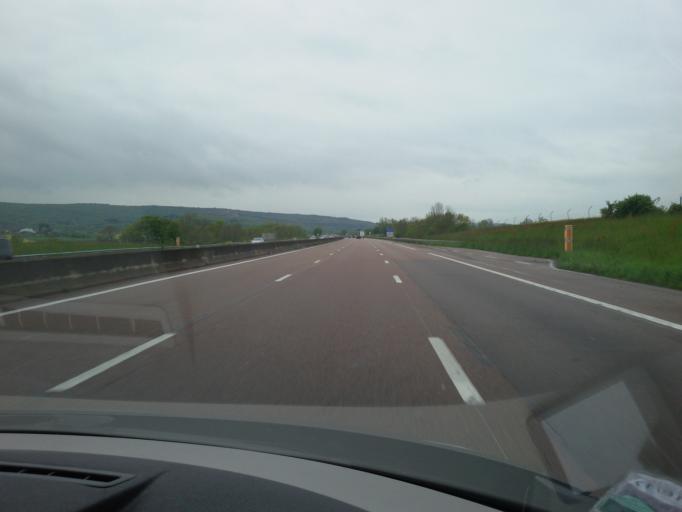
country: FR
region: Bourgogne
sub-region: Departement de Saone-et-Loire
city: Tournus
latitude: 46.6015
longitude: 4.8874
